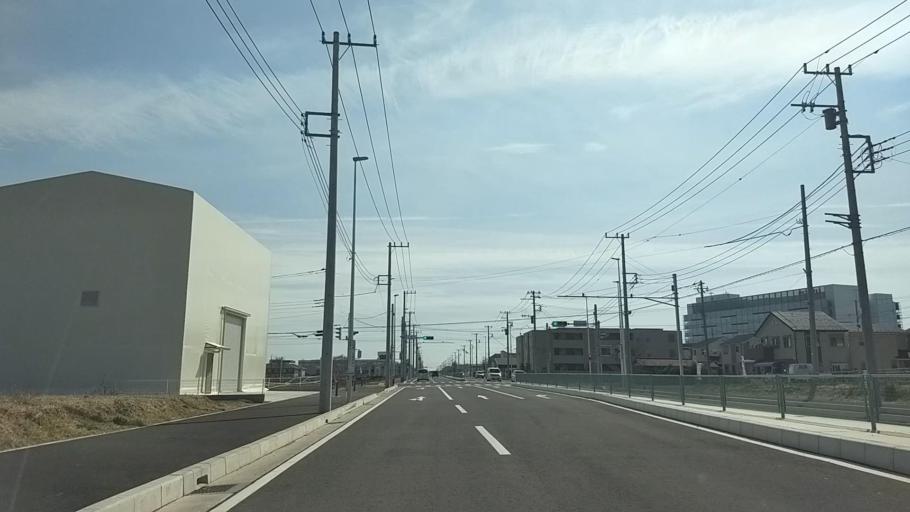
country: JP
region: Kanagawa
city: Fujisawa
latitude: 35.4059
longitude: 139.4541
